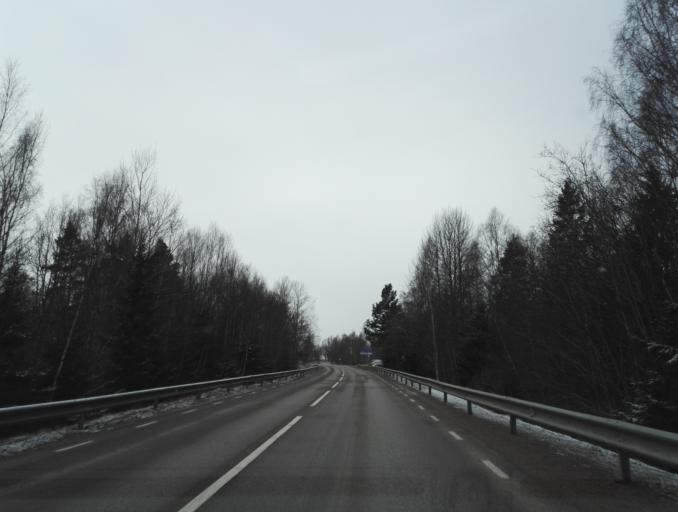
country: SE
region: Kalmar
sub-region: Hultsfreds Kommun
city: Virserum
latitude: 57.2965
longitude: 15.5694
